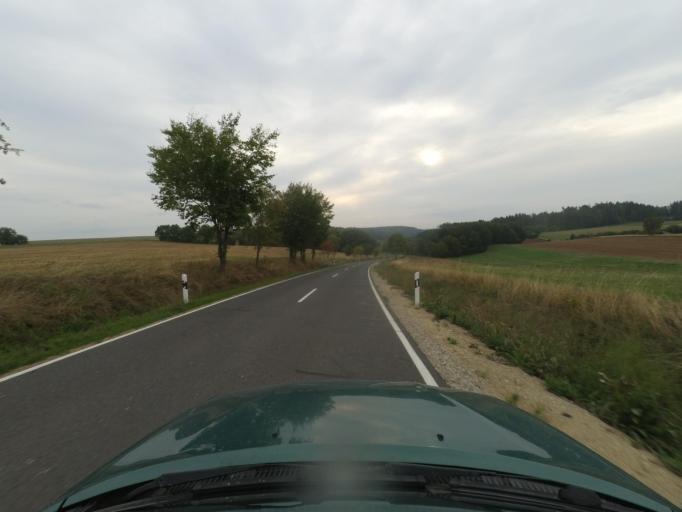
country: DE
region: Bavaria
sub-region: Upper Palatinate
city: Edelsfeld
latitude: 49.5789
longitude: 11.7012
